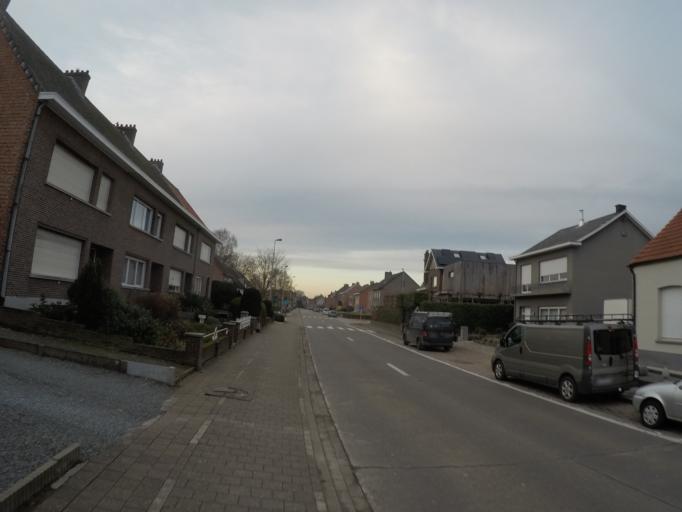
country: BE
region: Flanders
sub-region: Provincie Antwerpen
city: Berlaar
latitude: 51.1131
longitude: 4.6510
